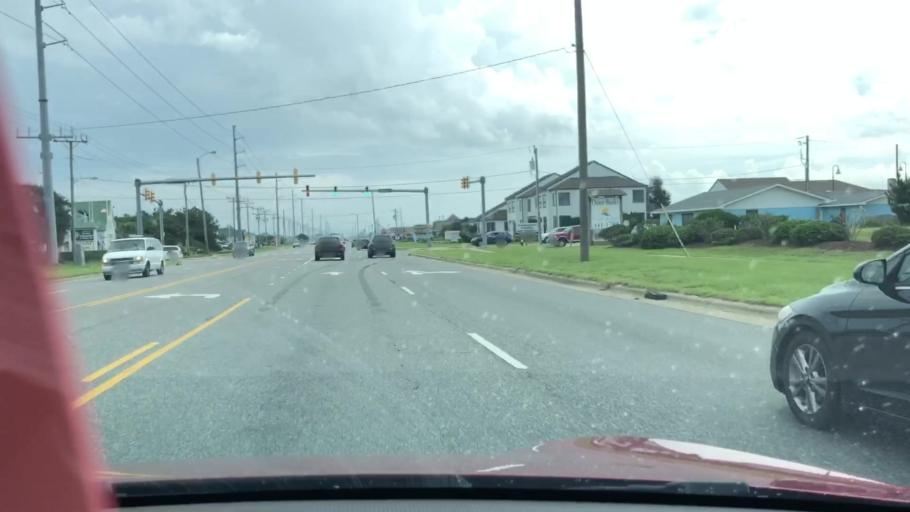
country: US
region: North Carolina
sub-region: Dare County
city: Kill Devil Hills
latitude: 36.0522
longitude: -75.6845
